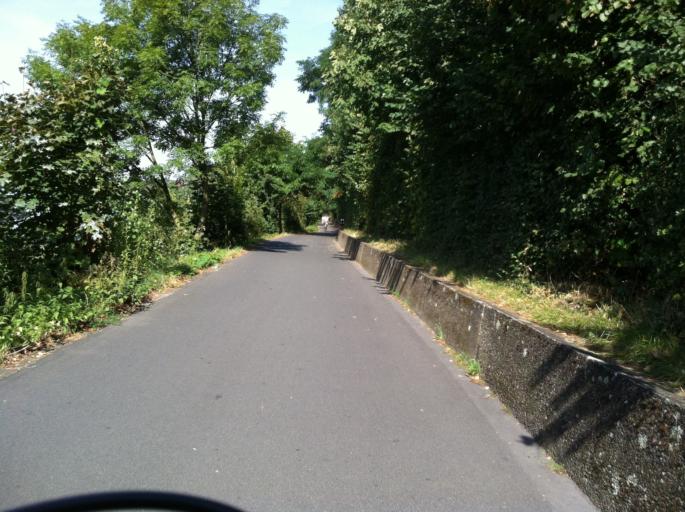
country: DE
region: North Rhine-Westphalia
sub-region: Regierungsbezirk Koln
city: Porz am Rhein
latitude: 50.8873
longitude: 7.0530
